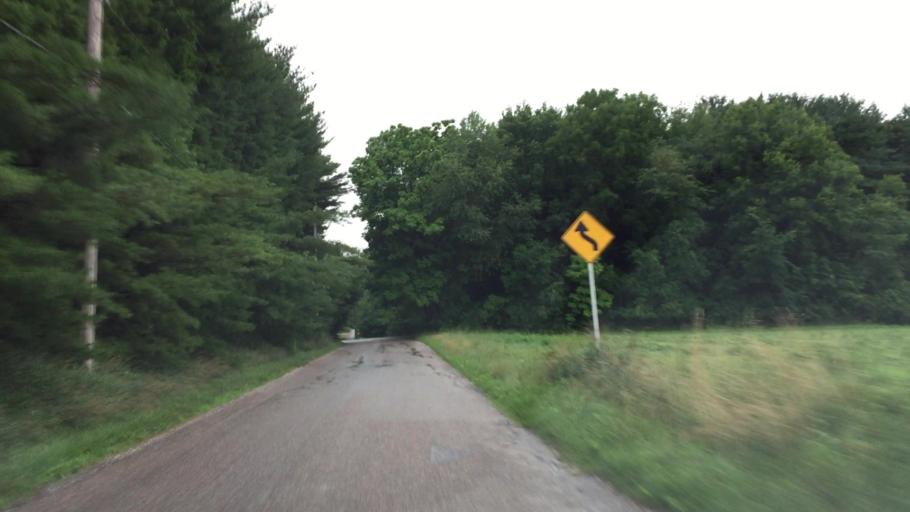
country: US
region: Illinois
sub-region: Hancock County
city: Nauvoo
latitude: 40.5403
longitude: -91.3760
